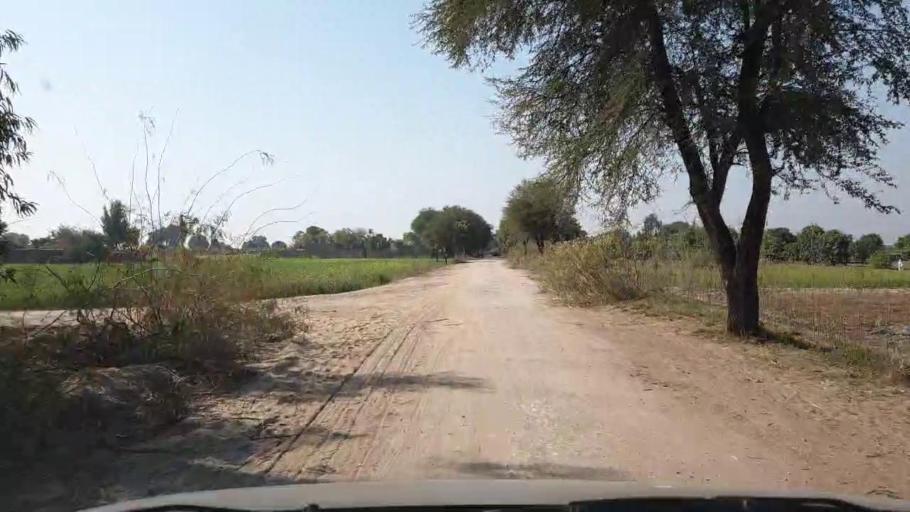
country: PK
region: Sindh
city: Tando Jam
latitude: 25.4382
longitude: 68.6227
